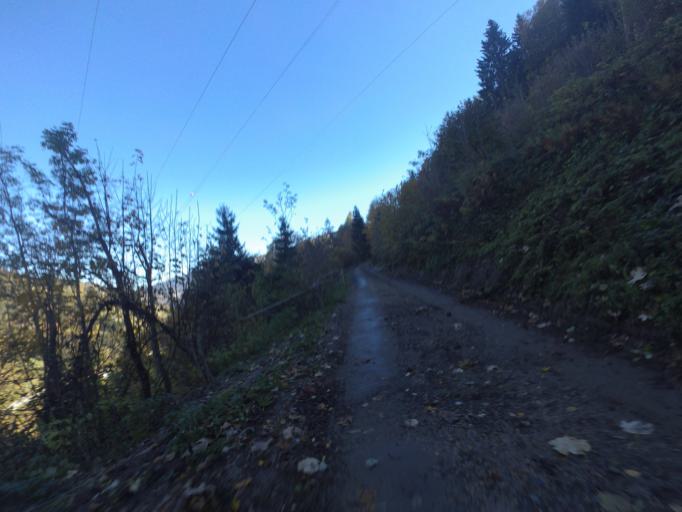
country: AT
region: Salzburg
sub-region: Politischer Bezirk Sankt Johann im Pongau
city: Sankt Johann im Pongau
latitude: 47.3308
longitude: 13.2152
